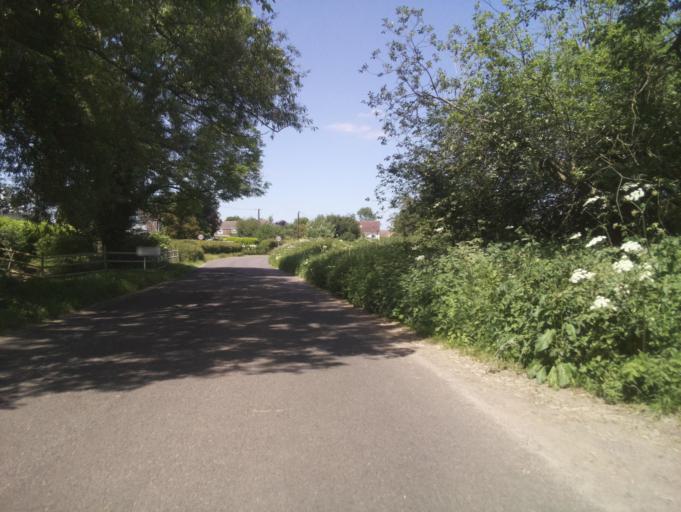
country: GB
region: England
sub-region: Wiltshire
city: Bremhill
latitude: 51.5050
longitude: -2.0515
